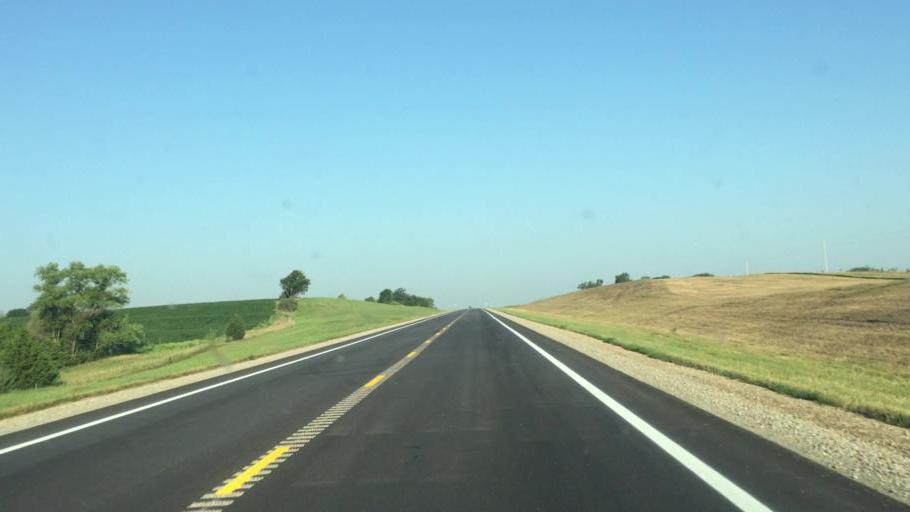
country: US
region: Kansas
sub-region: Doniphan County
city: Highland
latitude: 39.8412
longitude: -95.3820
